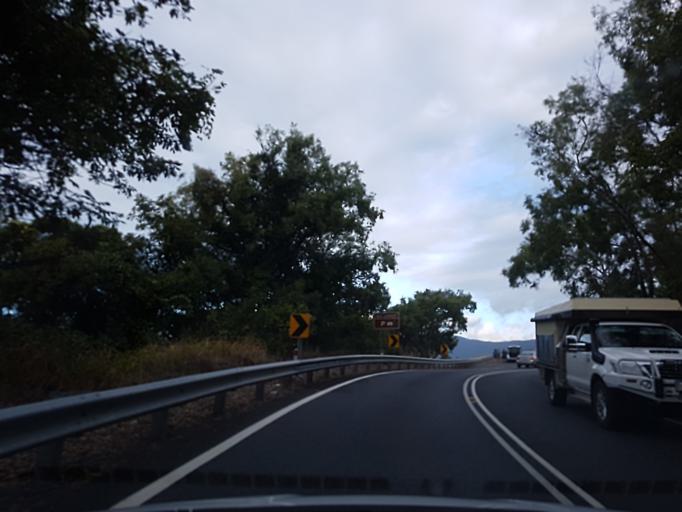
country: AU
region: Queensland
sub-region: Cairns
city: Palm Cove
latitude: -16.6454
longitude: 145.5654
